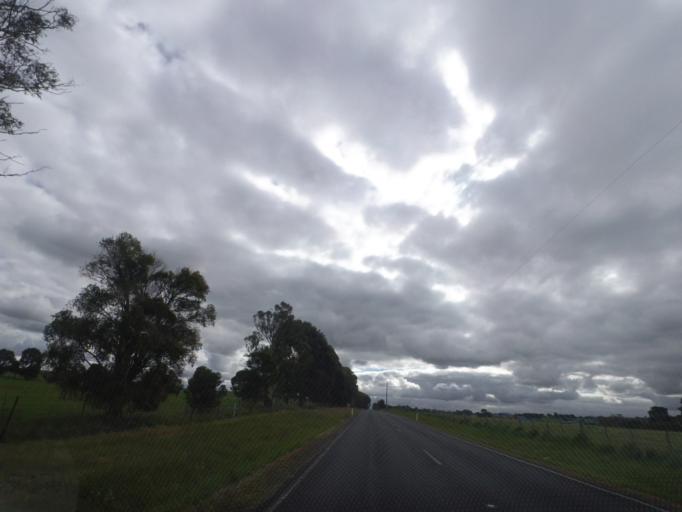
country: AU
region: Victoria
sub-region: Whittlesea
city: Whittlesea
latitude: -37.5251
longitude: 145.0804
